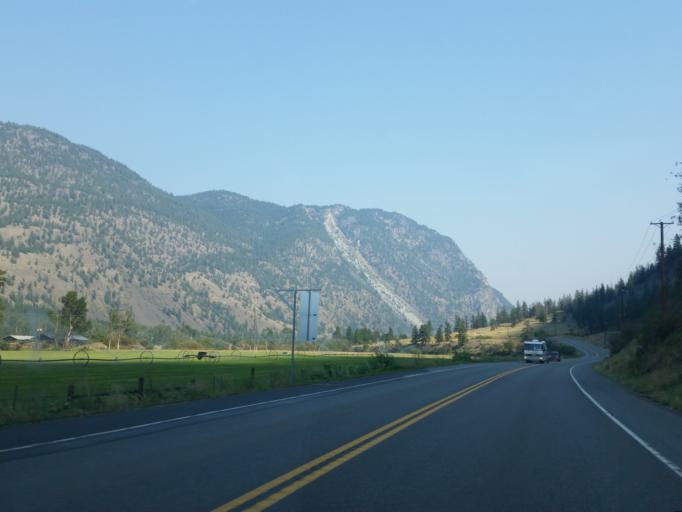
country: CA
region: British Columbia
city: Oliver
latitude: 49.2715
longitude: -120.0204
